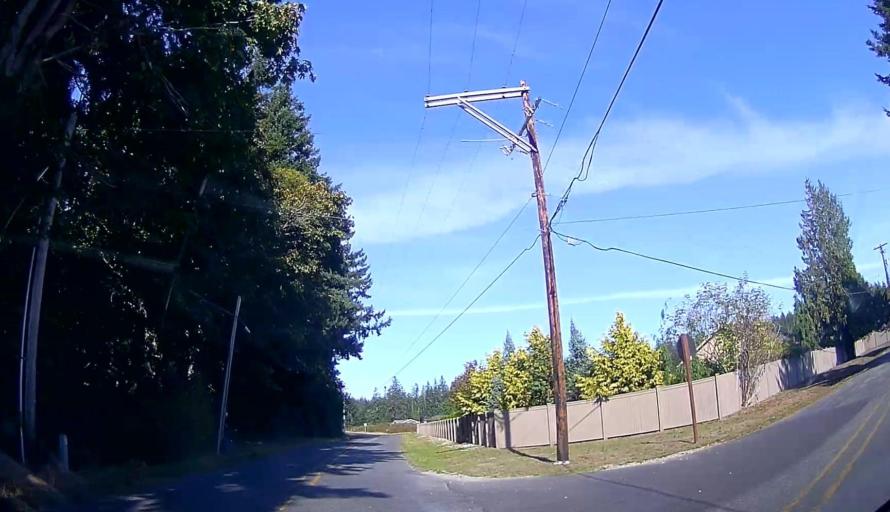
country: US
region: Washington
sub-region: Island County
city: Camano
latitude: 48.1775
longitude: -122.5201
